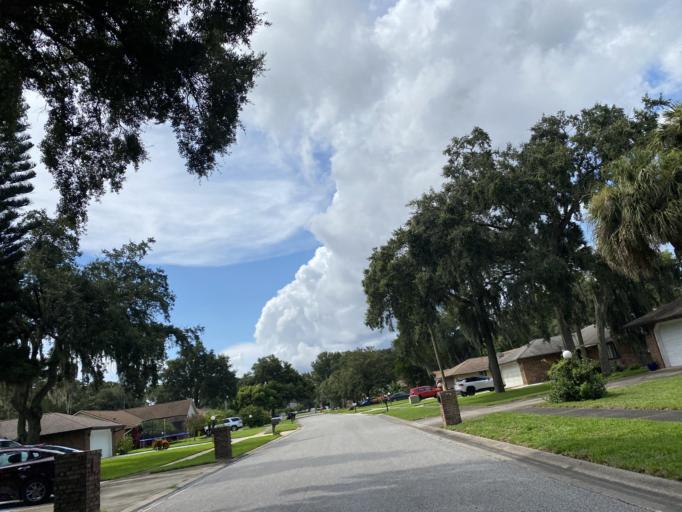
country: US
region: Florida
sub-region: Volusia County
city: Port Orange
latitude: 29.1354
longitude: -81.0016
